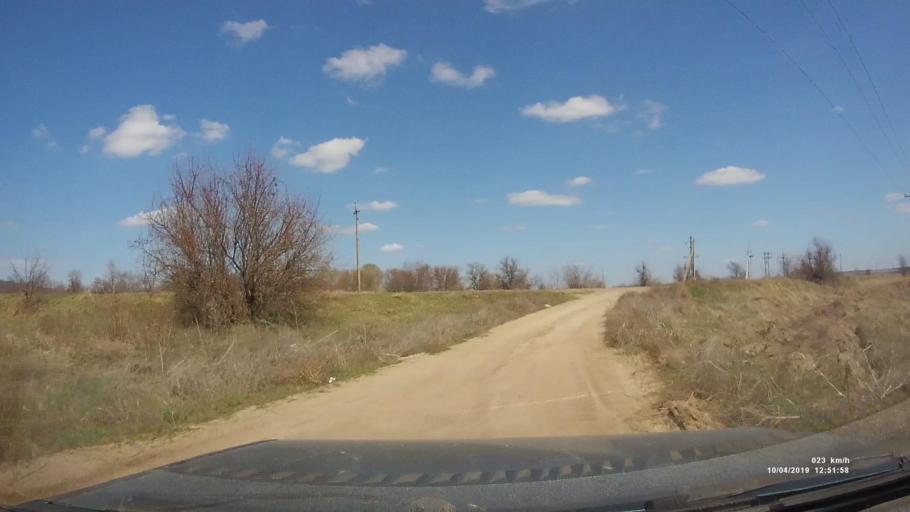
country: RU
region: Rostov
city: Kamensk-Shakhtinskiy
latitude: 48.3609
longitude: 40.2172
